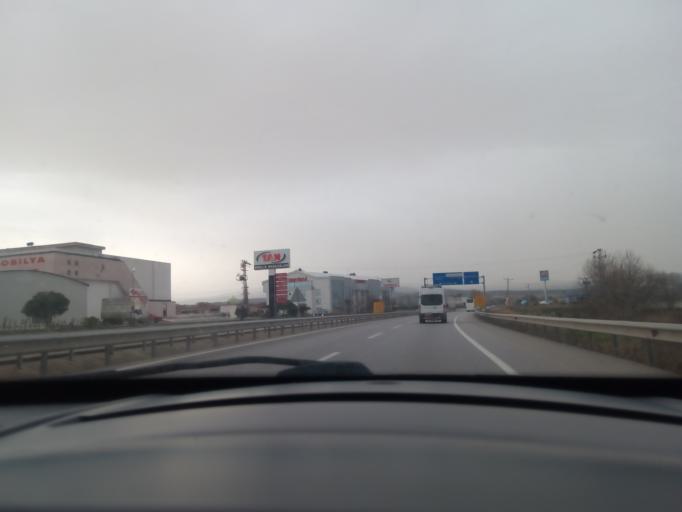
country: TR
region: Bursa
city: Tatkavakli
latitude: 40.0377
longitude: 28.3767
